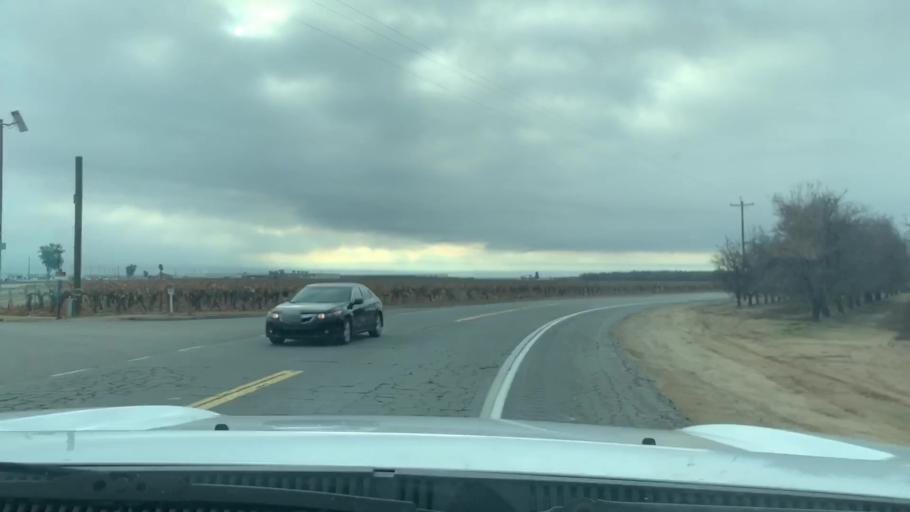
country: US
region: California
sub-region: Kern County
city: Rosedale
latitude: 35.4899
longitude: -119.1530
